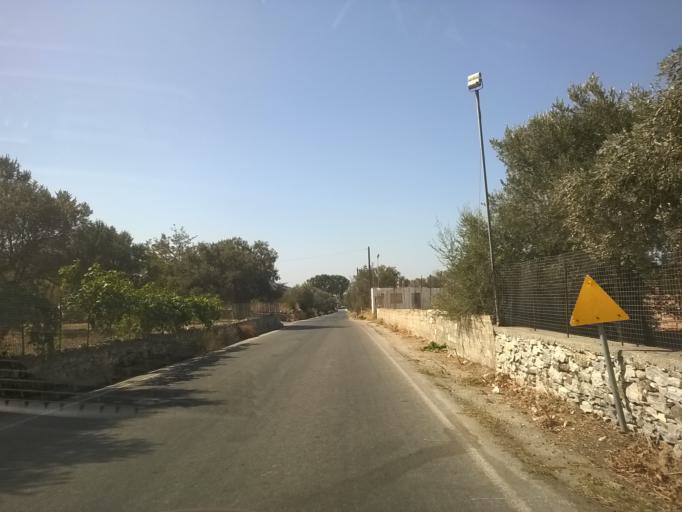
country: GR
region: South Aegean
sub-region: Nomos Kykladon
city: Filotion
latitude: 37.0662
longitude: 25.4877
